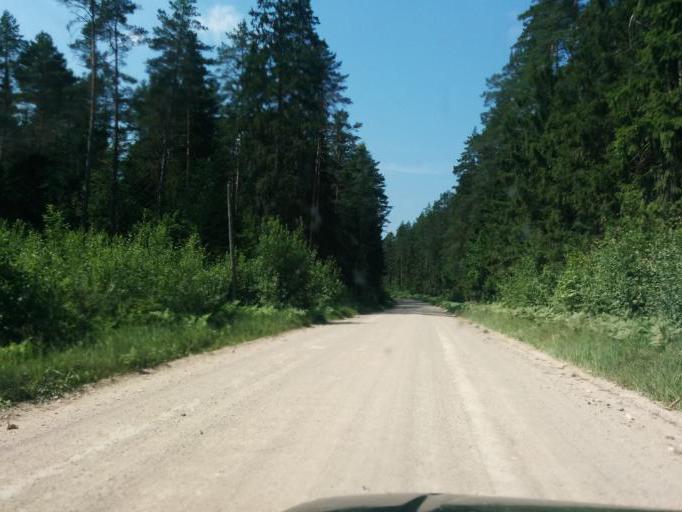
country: LV
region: Baldone
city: Baldone
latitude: 56.7478
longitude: 24.4507
